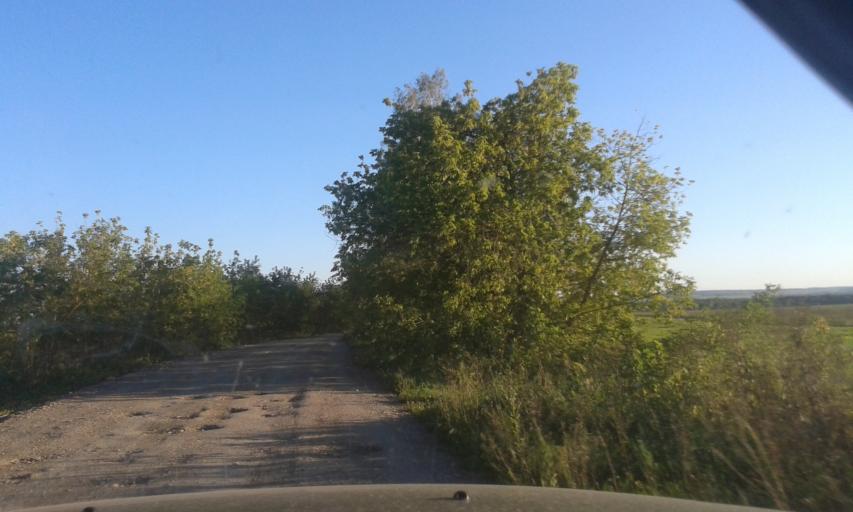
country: RU
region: Tula
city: Krapivna
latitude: 54.1316
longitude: 37.1571
